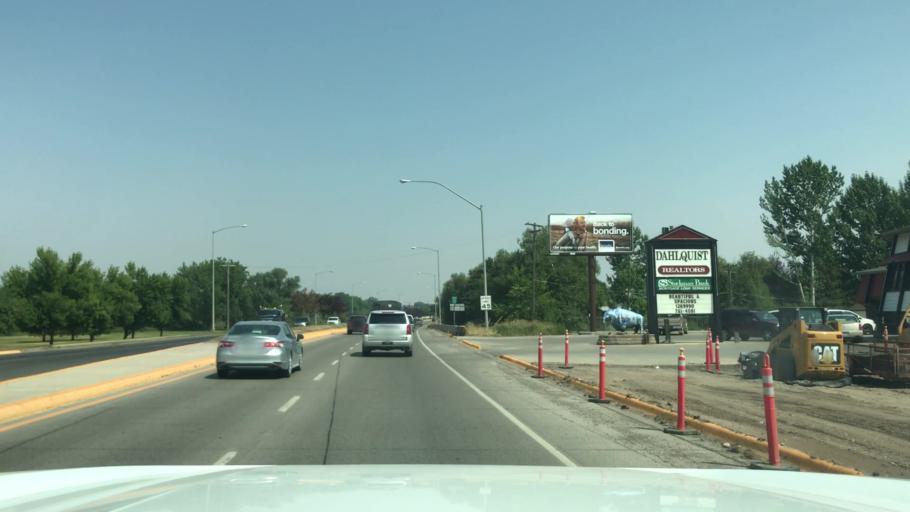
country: US
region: Montana
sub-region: Cascade County
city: Great Falls
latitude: 47.4906
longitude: -111.3271
